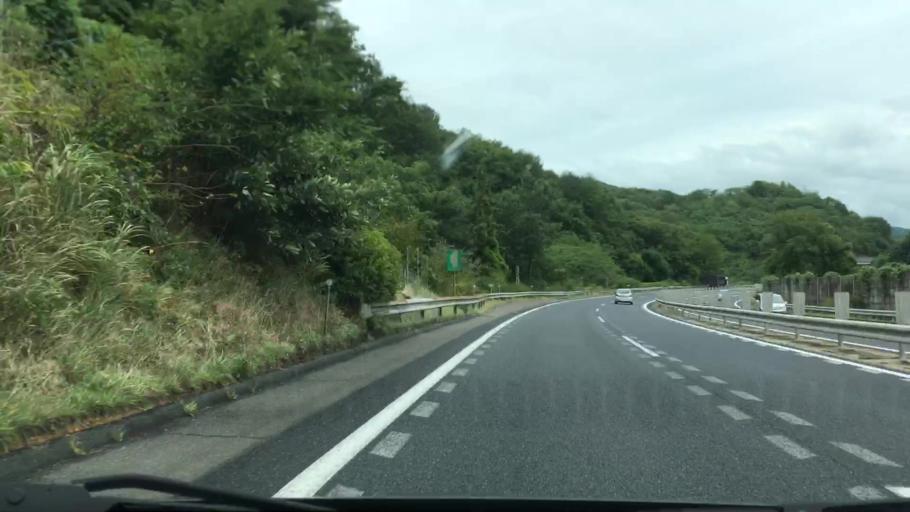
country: JP
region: Hyogo
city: Yamazakicho-nakabirose
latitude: 35.0074
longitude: 134.3249
